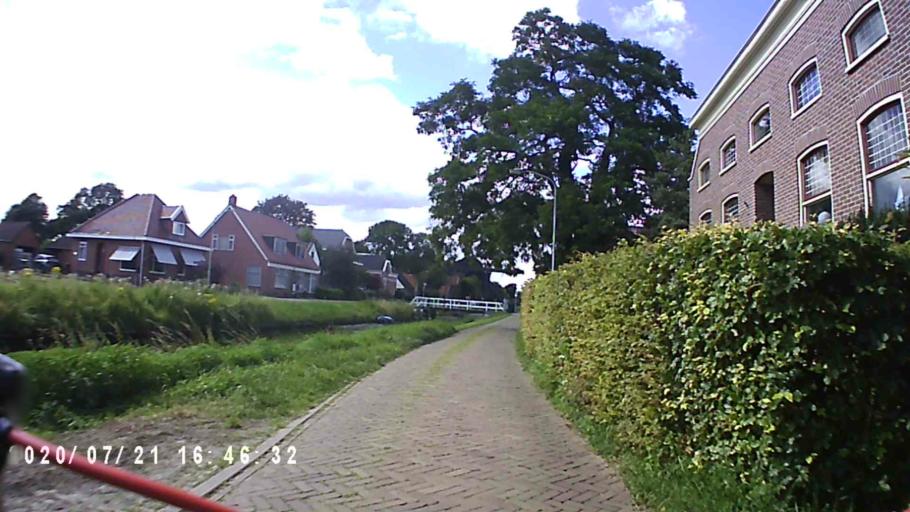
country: NL
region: Groningen
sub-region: Gemeente Hoogezand-Sappemeer
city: Hoogezand
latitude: 53.1129
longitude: 6.7793
